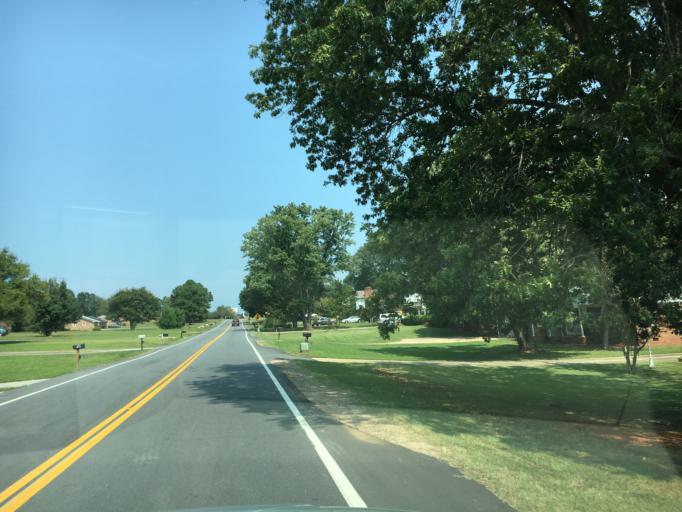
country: US
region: South Carolina
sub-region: Spartanburg County
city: Valley Falls
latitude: 35.0186
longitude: -81.9492
